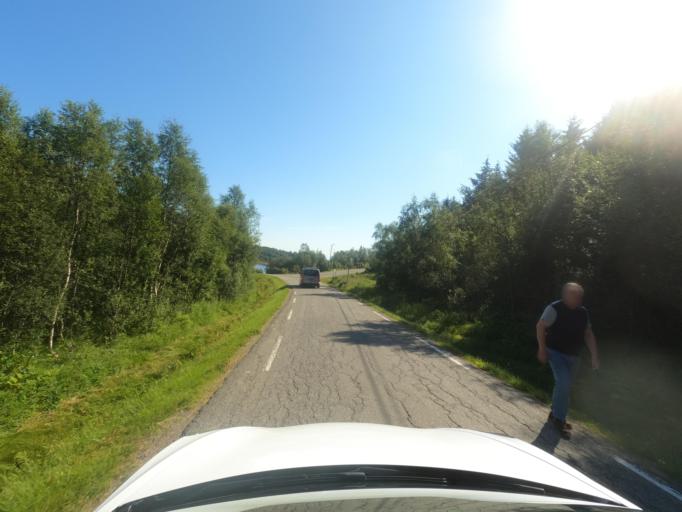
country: NO
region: Nordland
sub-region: Hadsel
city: Stokmarknes
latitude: 68.3029
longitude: 15.0391
